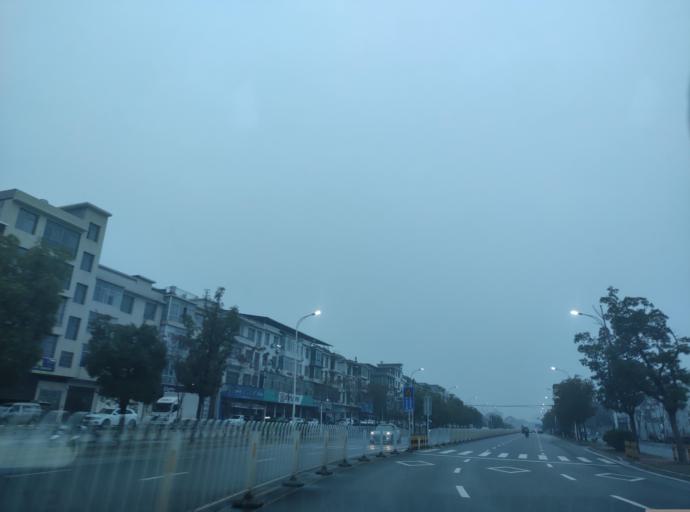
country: CN
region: Jiangxi Sheng
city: Pingxiang
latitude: 27.6686
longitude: 113.8701
